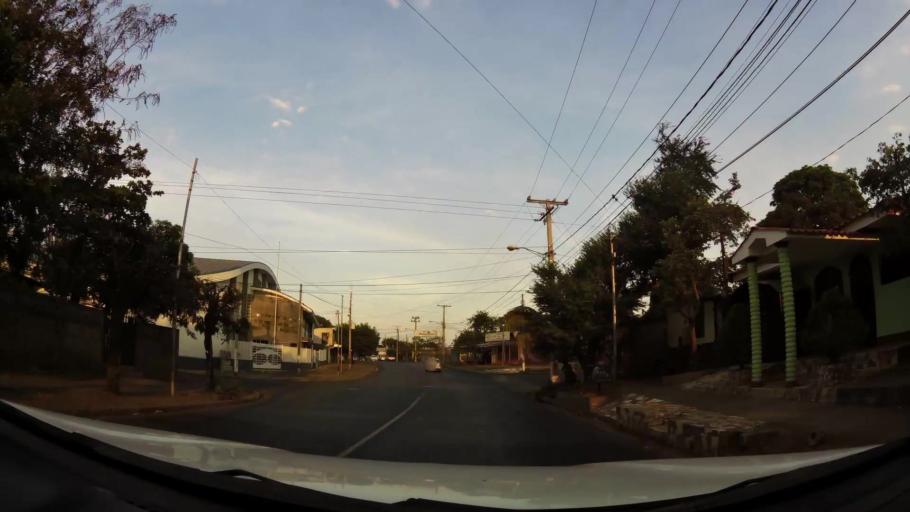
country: NI
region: Managua
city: Managua
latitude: 12.1414
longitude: -86.2436
